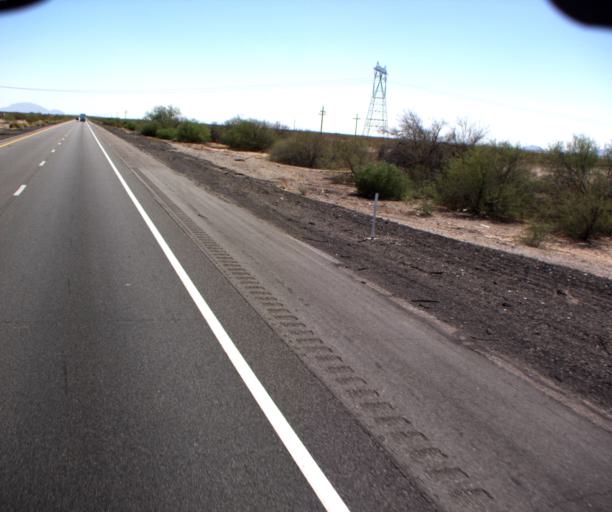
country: US
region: Arizona
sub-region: La Paz County
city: Salome
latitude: 33.5762
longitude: -113.4025
